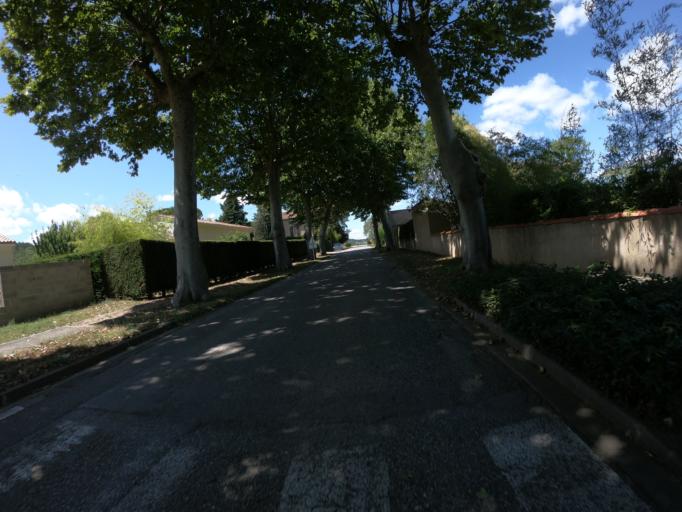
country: FR
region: Midi-Pyrenees
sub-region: Departement de l'Ariege
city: Verniolle
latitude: 43.0517
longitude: 1.7571
